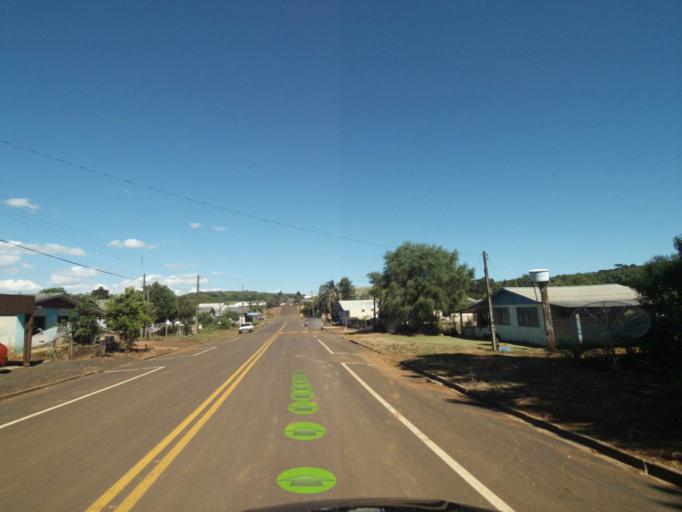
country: BR
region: Parana
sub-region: Coronel Vivida
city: Coronel Vivida
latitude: -26.1450
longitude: -52.3883
